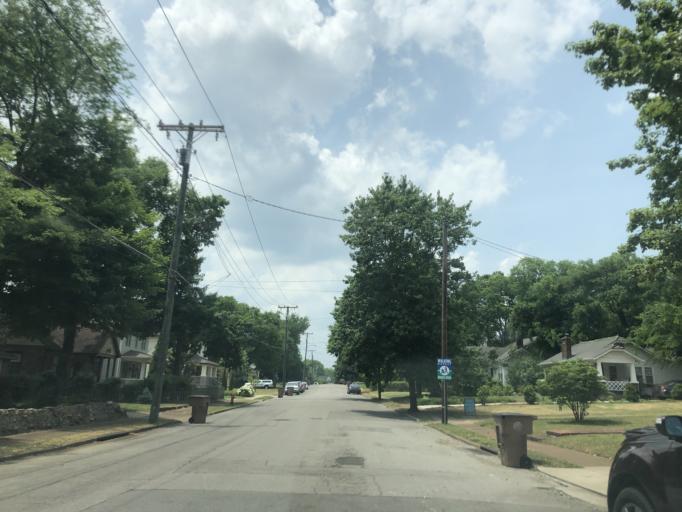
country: US
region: Tennessee
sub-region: Davidson County
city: Nashville
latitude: 36.1301
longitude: -86.8081
